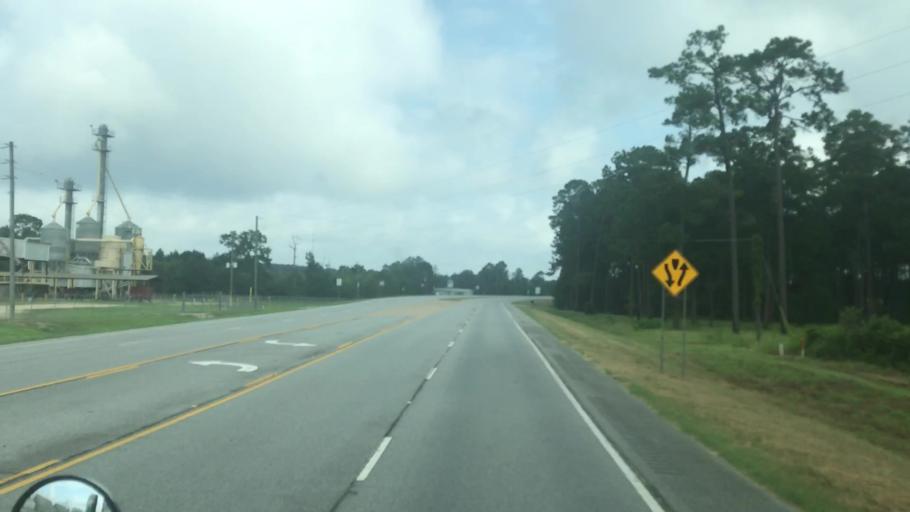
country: US
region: Georgia
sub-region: Miller County
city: Colquitt
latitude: 31.1724
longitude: -84.7574
